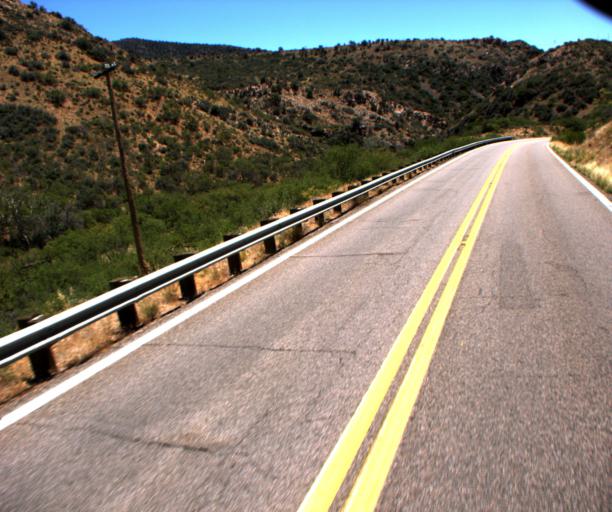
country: US
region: Arizona
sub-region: Gila County
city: Globe
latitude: 33.2113
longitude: -110.7979
